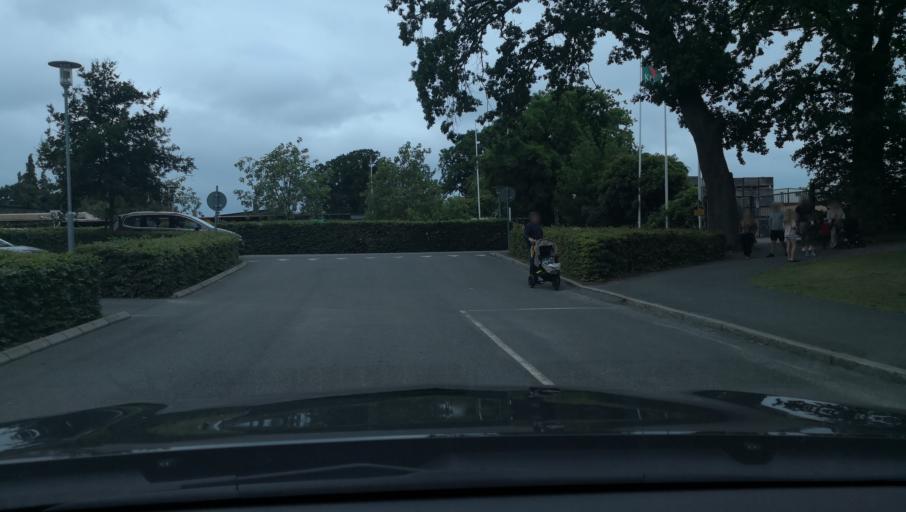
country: SE
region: Skane
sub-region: Simrishamns Kommun
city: Kivik
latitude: 55.6723
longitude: 14.2682
